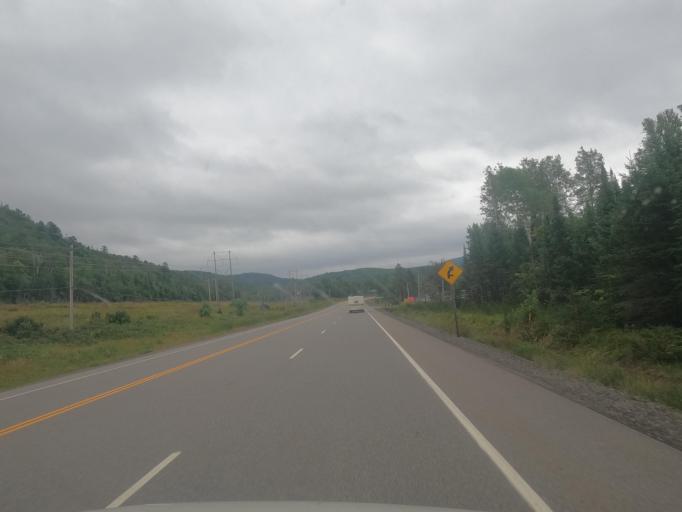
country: CA
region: Ontario
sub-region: Algoma
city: Sault Ste. Marie
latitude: 46.8944
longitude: -84.3669
